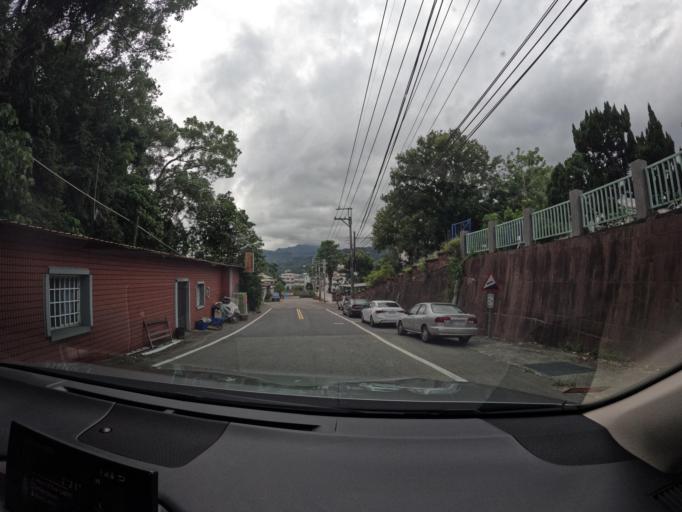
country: TW
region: Taiwan
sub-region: Miaoli
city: Miaoli
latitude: 24.4272
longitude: 120.8721
